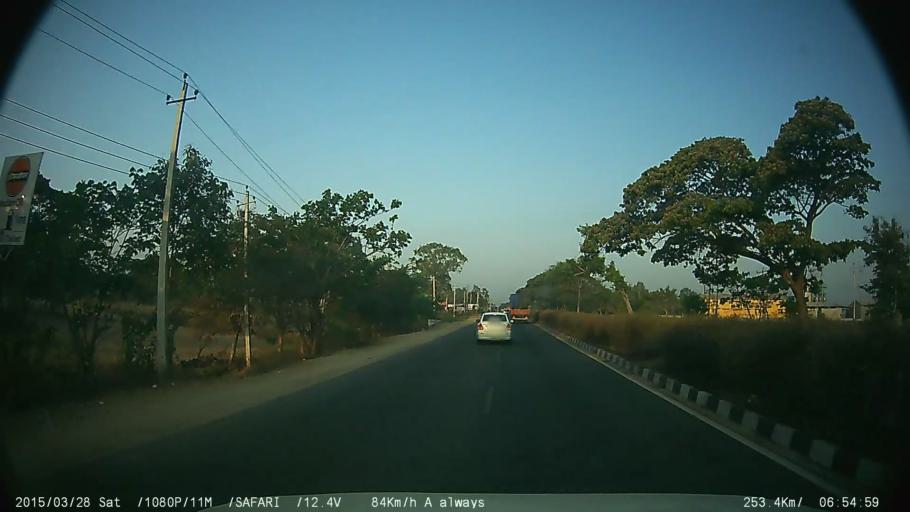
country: IN
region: Karnataka
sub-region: Mandya
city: Maddur
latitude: 12.5766
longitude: 77.0211
